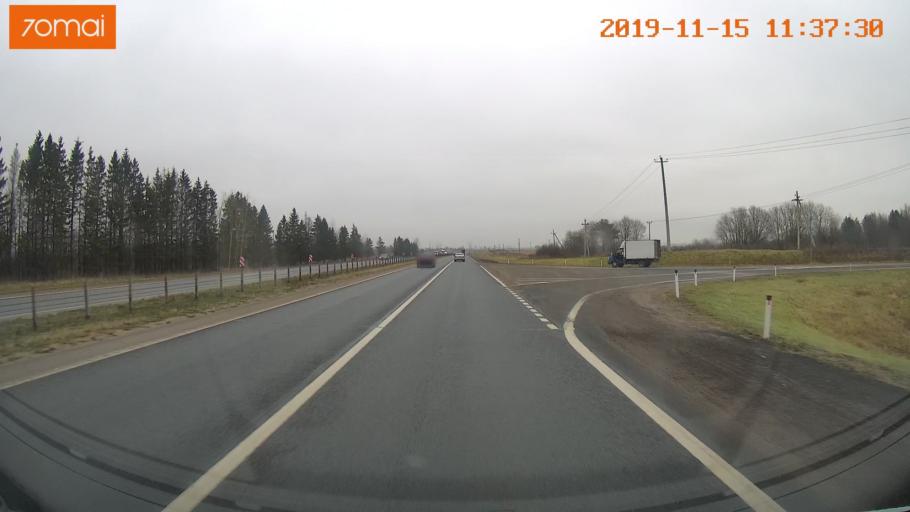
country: RU
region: Vologda
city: Molochnoye
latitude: 59.2058
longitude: 39.6742
